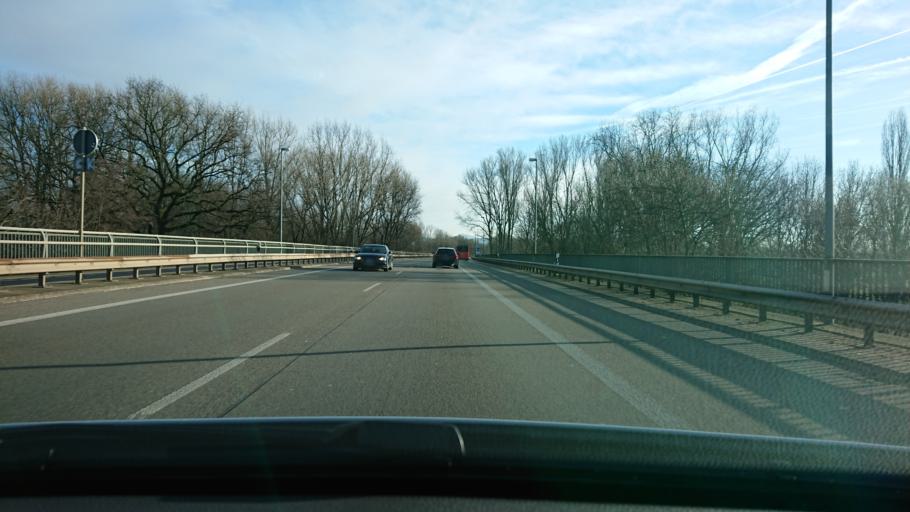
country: DE
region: North Rhine-Westphalia
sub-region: Regierungsbezirk Koln
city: Bonn
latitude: 50.7657
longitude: 7.1076
